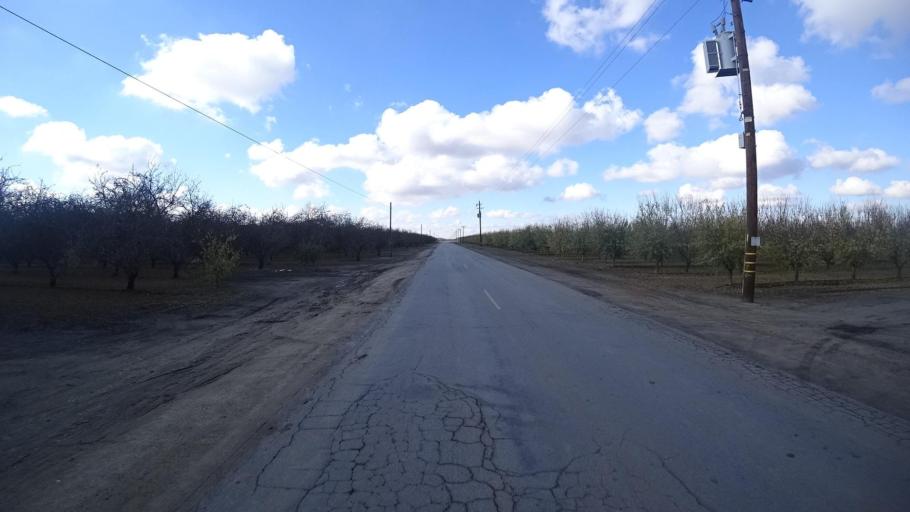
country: US
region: California
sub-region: Kern County
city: Wasco
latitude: 35.6886
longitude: -119.3259
